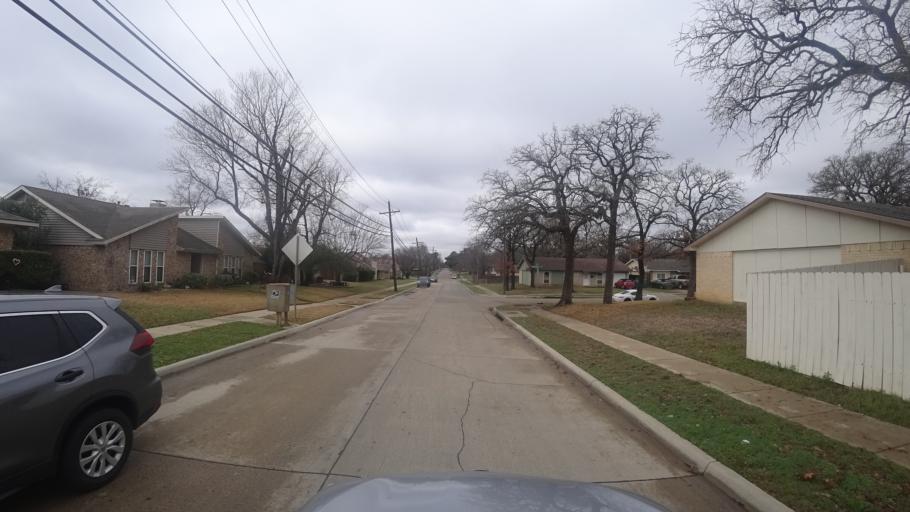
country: US
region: Texas
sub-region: Denton County
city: Lewisville
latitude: 33.0313
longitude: -97.0202
